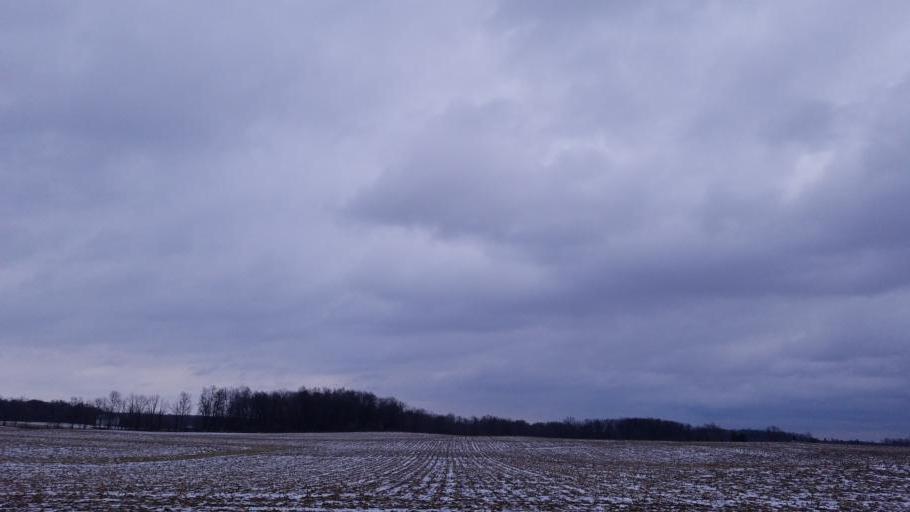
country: US
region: Ohio
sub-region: Richland County
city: Lexington
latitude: 40.6258
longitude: -82.6903
